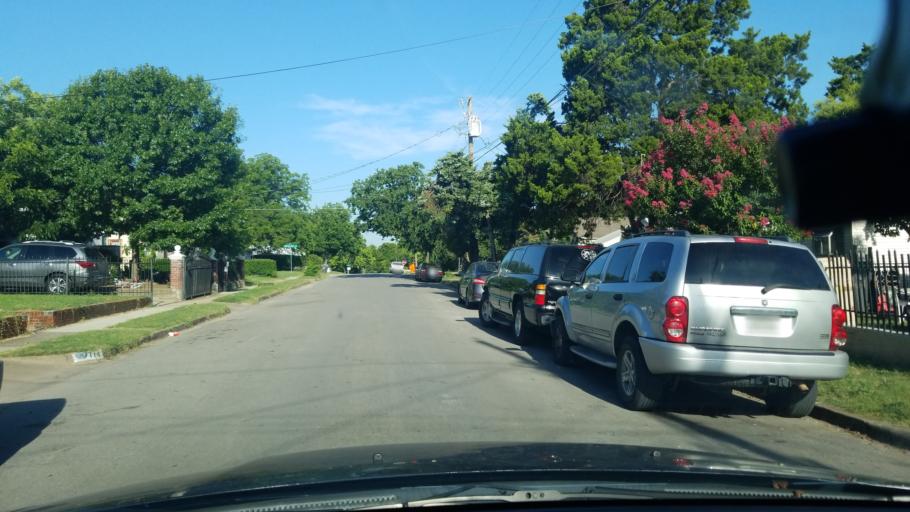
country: US
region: Texas
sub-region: Dallas County
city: Dallas
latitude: 32.7313
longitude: -96.8128
